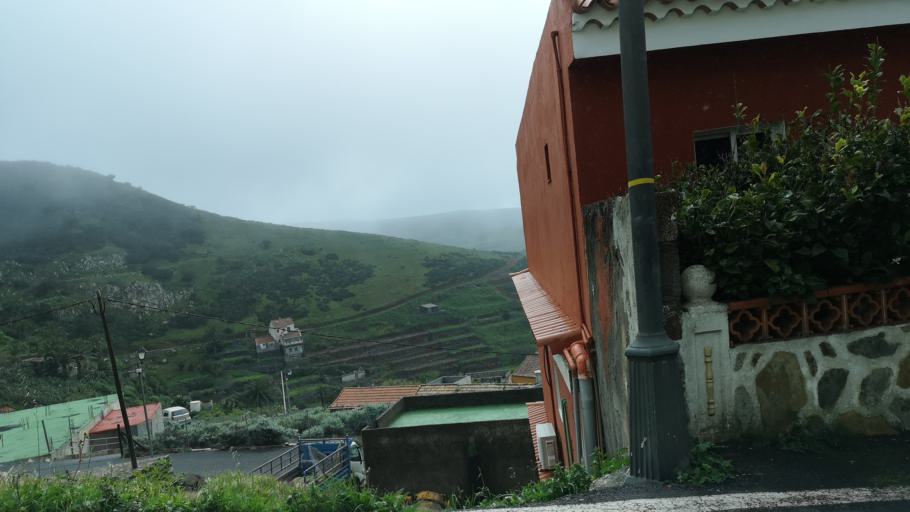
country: ES
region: Canary Islands
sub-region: Provincia de Santa Cruz de Tenerife
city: Vallehermosa
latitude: 28.1403
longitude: -17.3107
